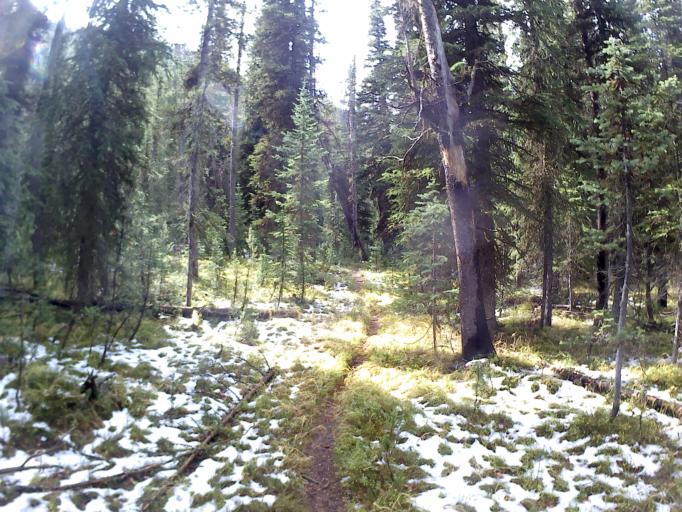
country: US
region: Montana
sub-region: Gallatin County
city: West Yellowstone
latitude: 44.4321
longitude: -110.7418
